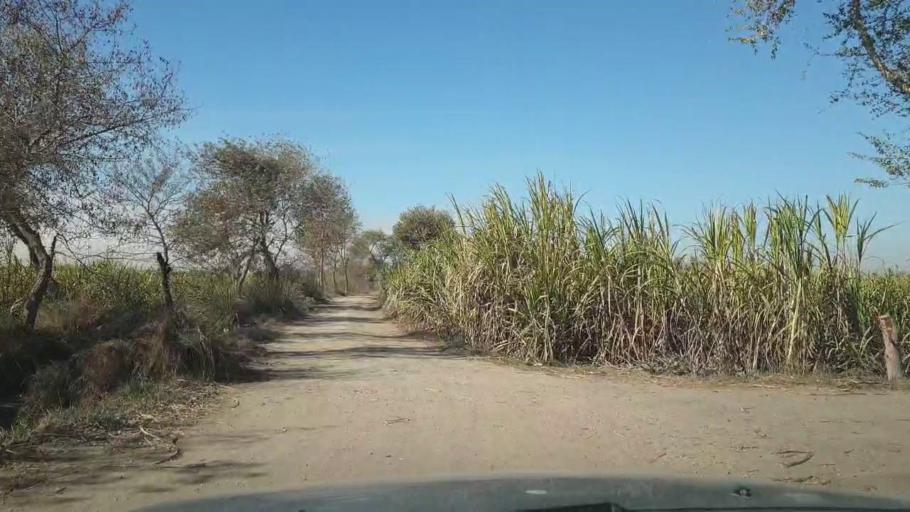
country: PK
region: Sindh
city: Ghotki
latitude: 28.0375
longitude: 69.2774
